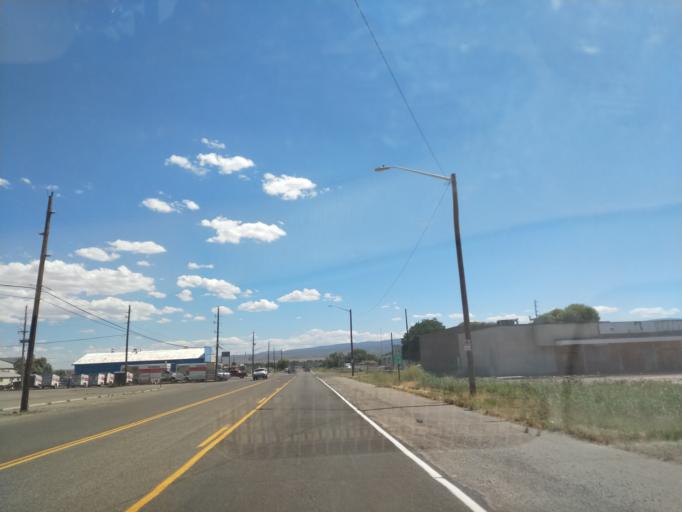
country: US
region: Colorado
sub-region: Mesa County
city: Grand Junction
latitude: 39.0766
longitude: -108.5337
